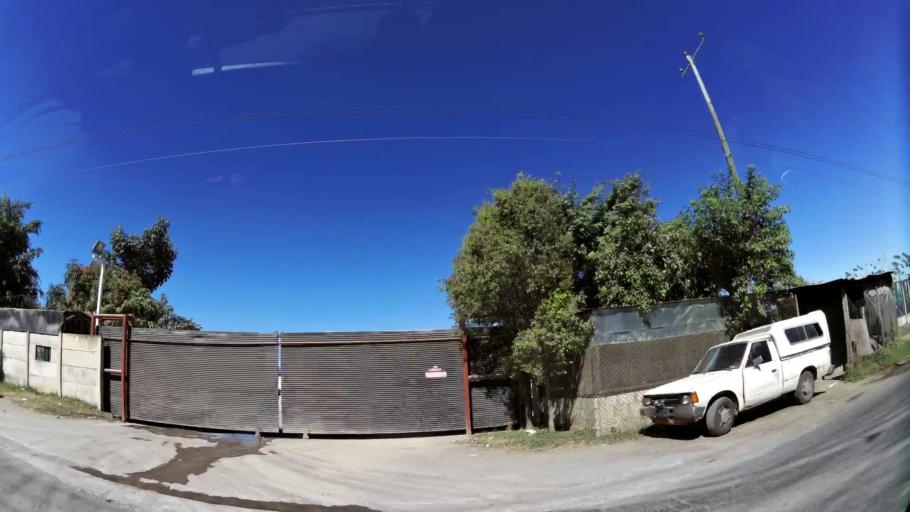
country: SV
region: La Libertad
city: San Juan Opico
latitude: 13.7960
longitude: -89.3665
